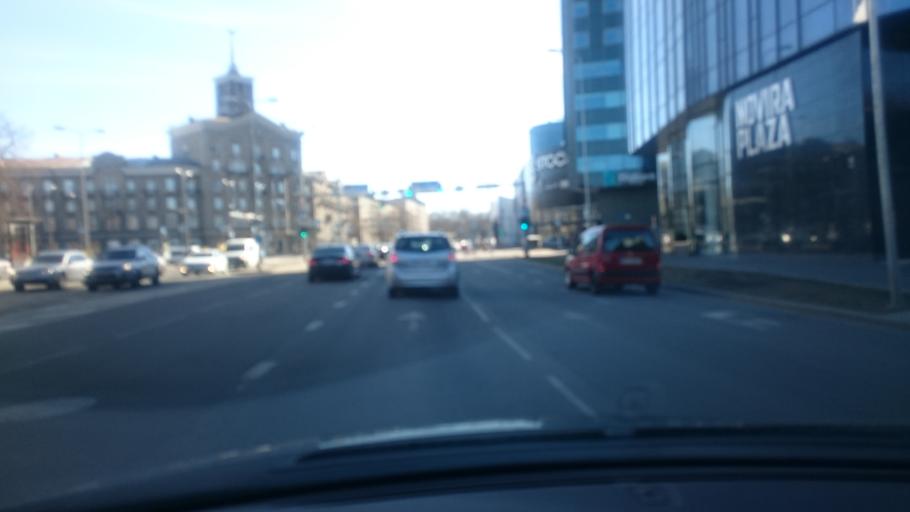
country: EE
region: Harju
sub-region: Tallinna linn
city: Tallinn
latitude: 59.4336
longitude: 24.7636
